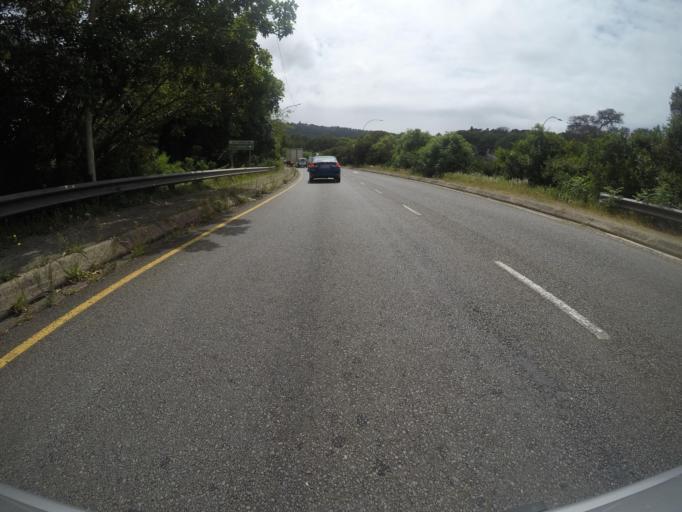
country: ZA
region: Eastern Cape
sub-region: Buffalo City Metropolitan Municipality
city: East London
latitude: -32.9760
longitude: 27.9205
